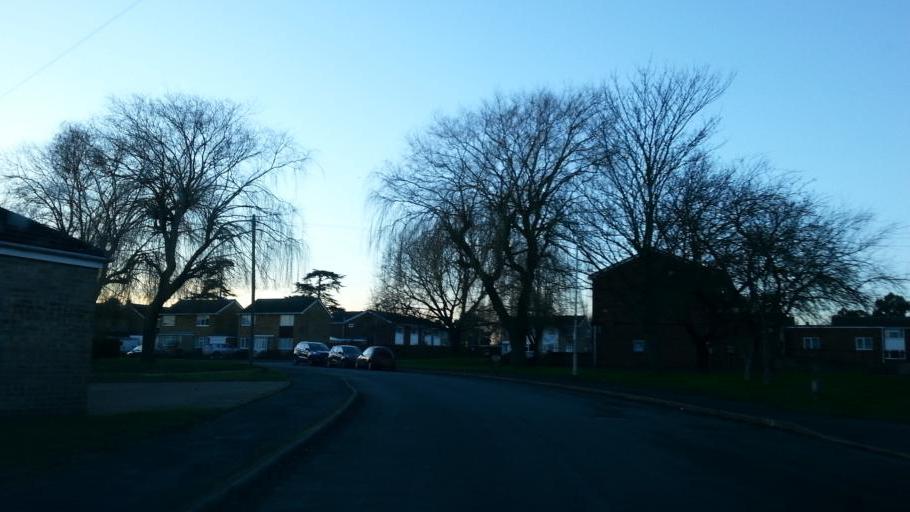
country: GB
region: England
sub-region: Cambridgeshire
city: Hemingford Grey
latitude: 52.2972
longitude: -0.0643
